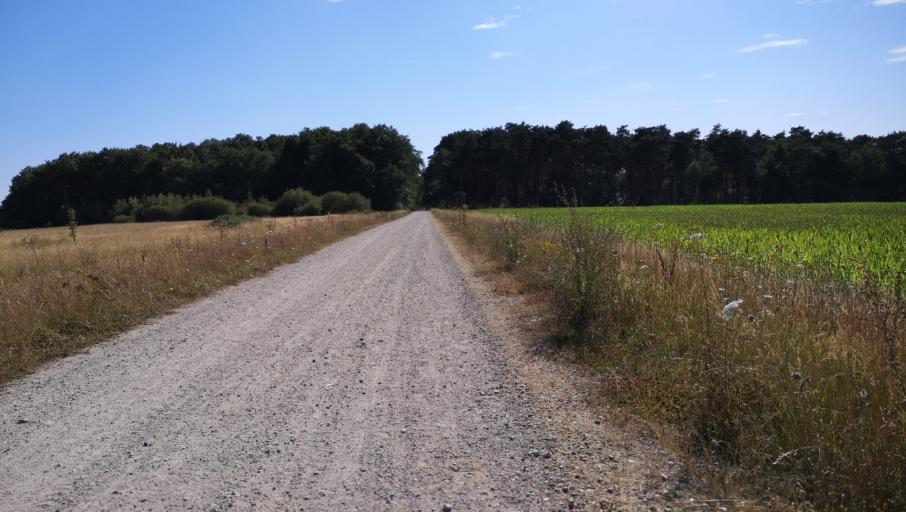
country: FR
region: Centre
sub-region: Departement du Loiret
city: Marigny-les-Usages
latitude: 47.9521
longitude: 2.0031
